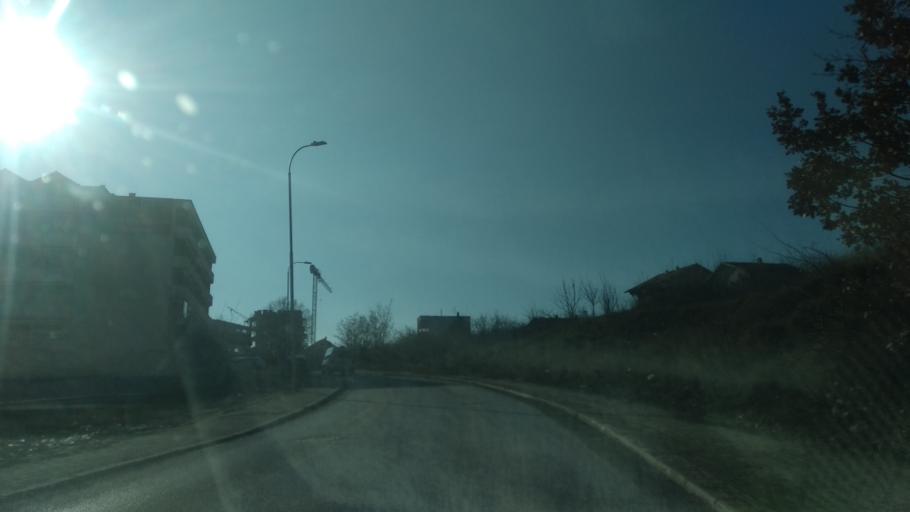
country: XK
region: Pristina
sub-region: Komuna e Prishtines
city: Pristina
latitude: 42.6355
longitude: 21.1581
